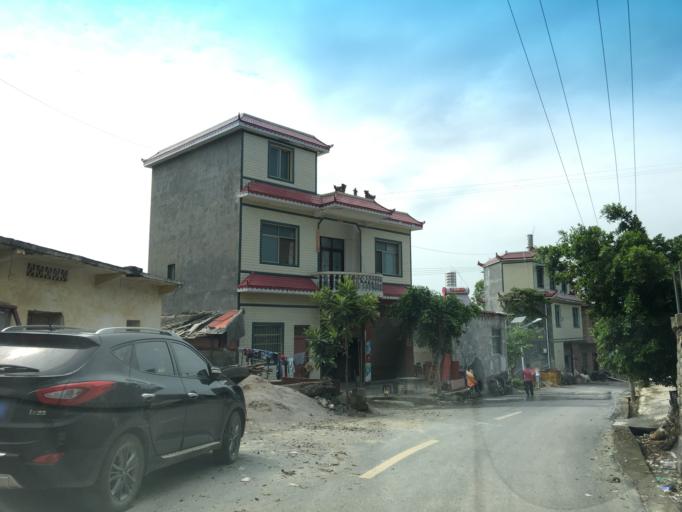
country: CN
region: Guangxi Zhuangzu Zizhiqu
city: Xinzhou
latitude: 24.8224
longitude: 105.6438
